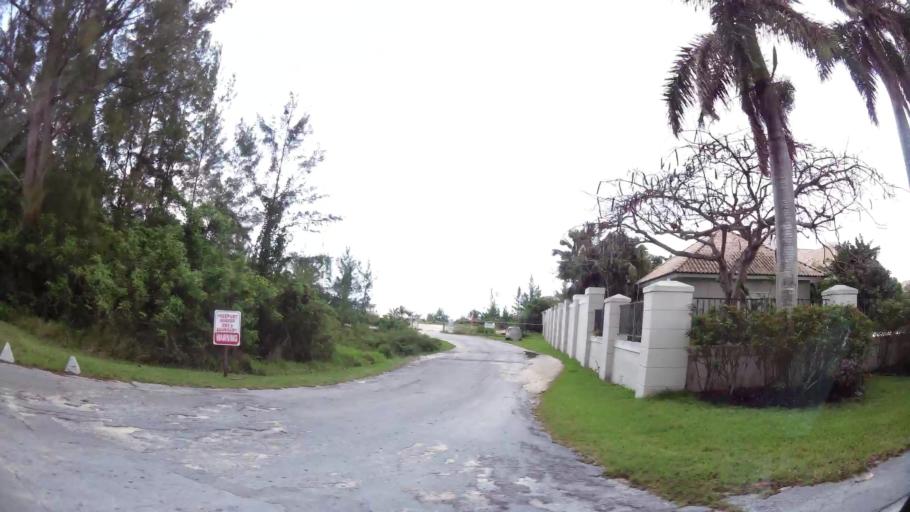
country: BS
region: Freeport
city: Lucaya
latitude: 26.5315
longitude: -78.5994
